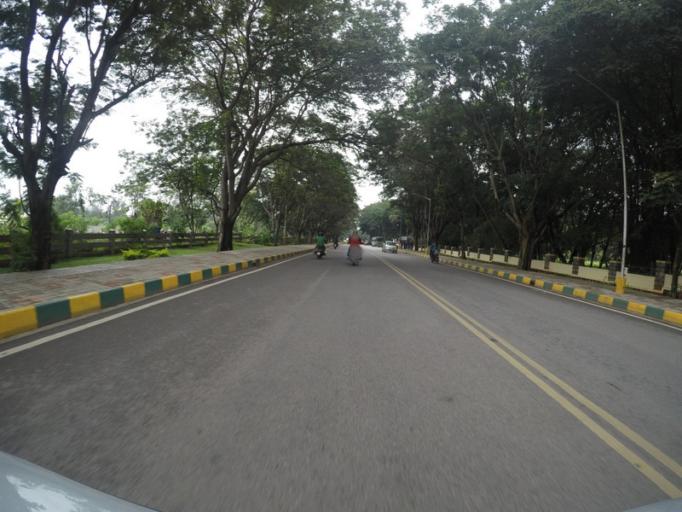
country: IN
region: Karnataka
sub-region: Bangalore Urban
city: Yelahanka
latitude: 13.0472
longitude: 77.5571
